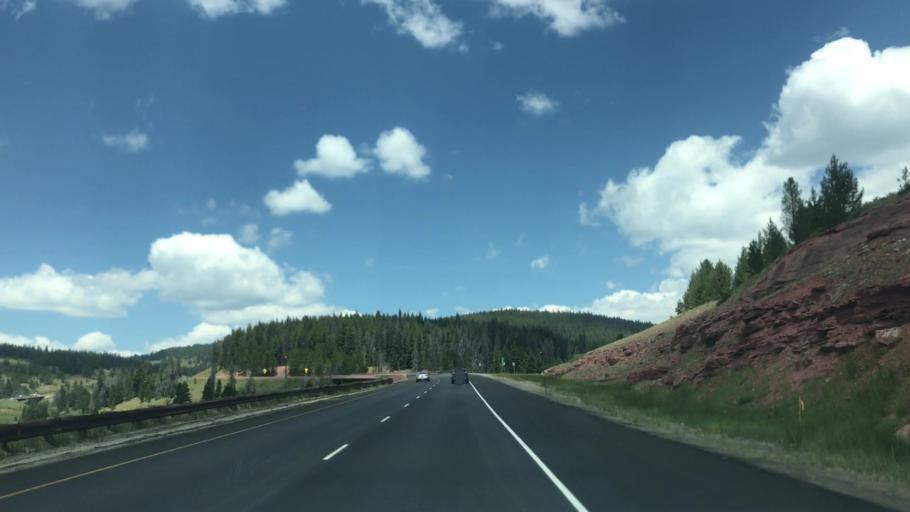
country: US
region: Colorado
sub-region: Summit County
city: Frisco
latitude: 39.5136
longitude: -106.2045
